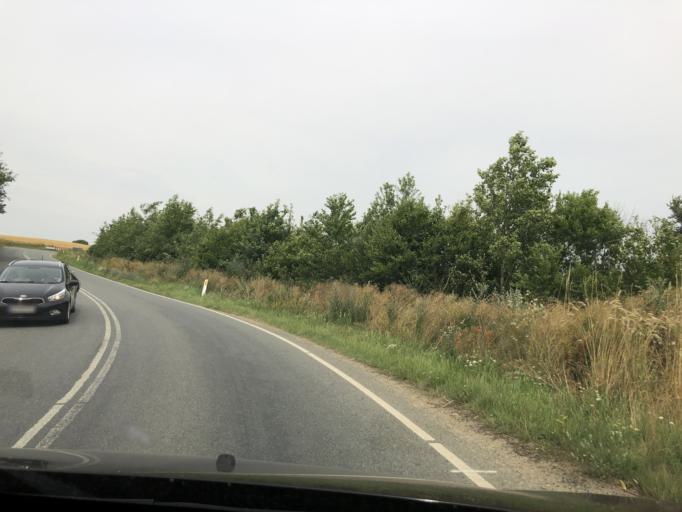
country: DK
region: South Denmark
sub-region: Assens Kommune
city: Glamsbjerg
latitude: 55.3049
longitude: 10.0533
